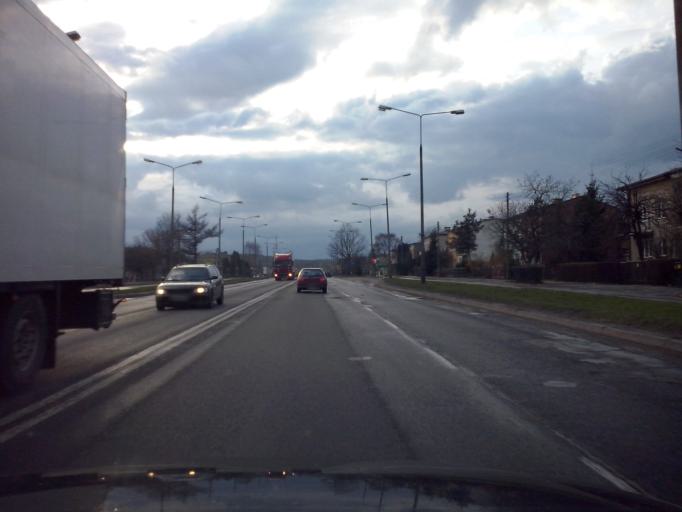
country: PL
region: Lublin Voivodeship
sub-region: Chelm
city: Chelm
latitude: 51.1453
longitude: 23.4502
